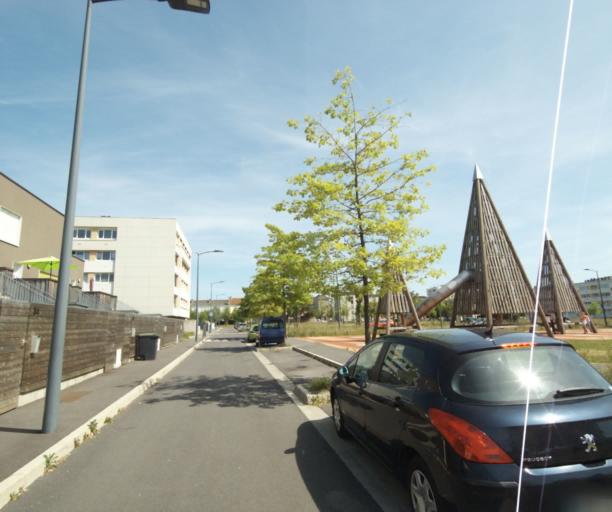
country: FR
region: Champagne-Ardenne
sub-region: Departement des Ardennes
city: Prix-les-Mezieres
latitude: 49.7651
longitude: 4.6886
